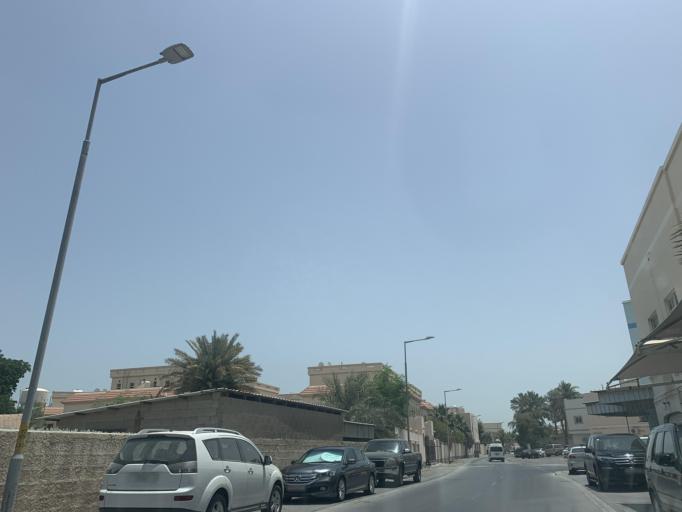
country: BH
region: Northern
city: Madinat `Isa
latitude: 26.1712
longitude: 50.5682
